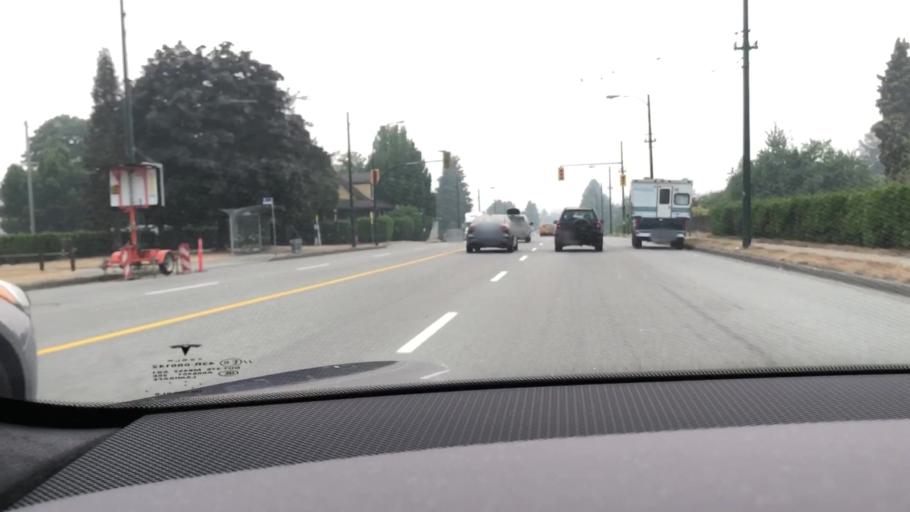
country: CA
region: British Columbia
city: Vancouver
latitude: 49.2330
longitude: -123.0936
